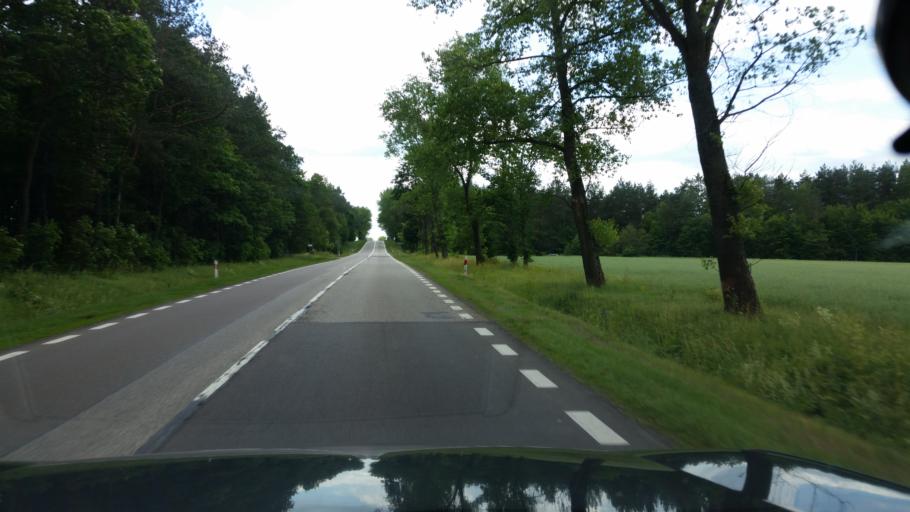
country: PL
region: Podlasie
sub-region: Powiat kolnenski
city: Stawiski
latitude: 53.3300
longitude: 22.1545
